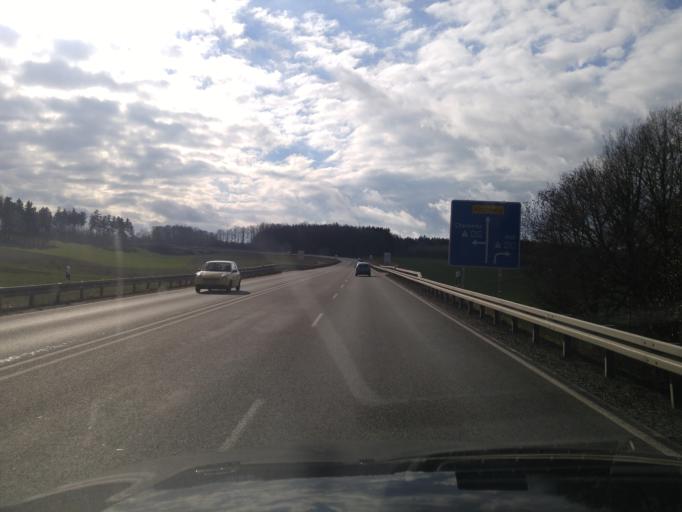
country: DE
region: Saxony
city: Hirschfeld
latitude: 50.6456
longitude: 12.4428
